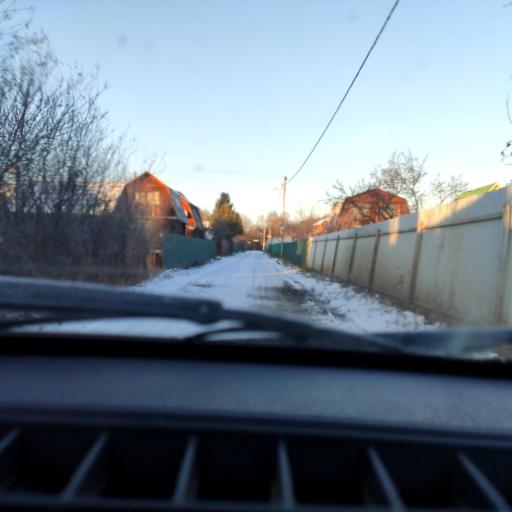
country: RU
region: Bashkortostan
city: Avdon
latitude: 54.6254
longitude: 55.7153
